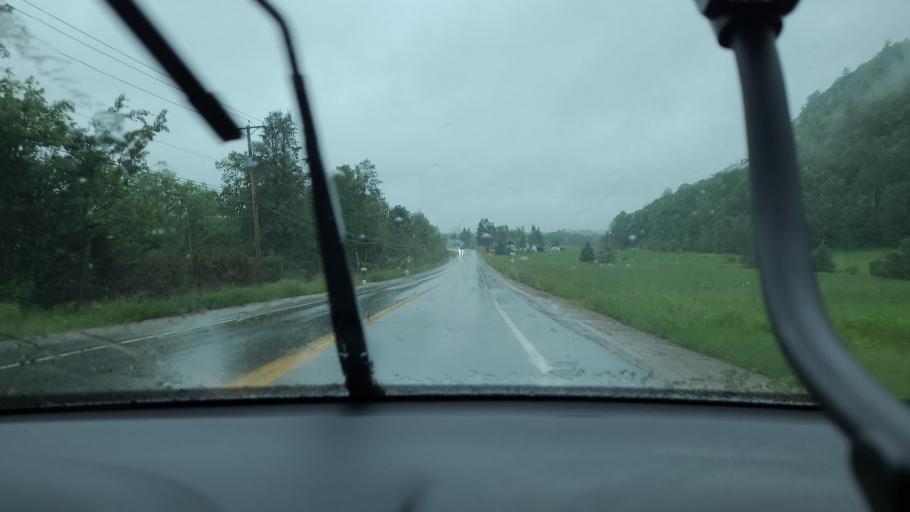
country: CA
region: Quebec
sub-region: Outaouais
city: Saint-Andre-Avellin
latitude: 45.8377
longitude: -75.0563
